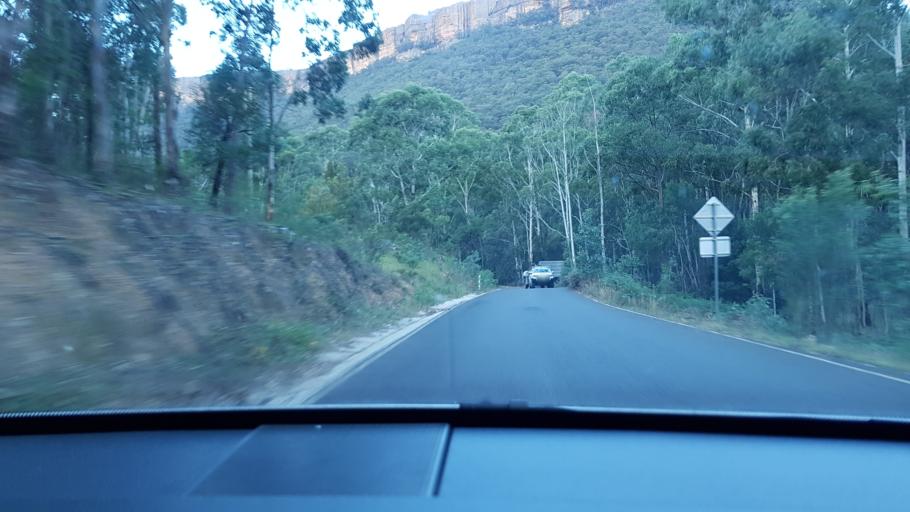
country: AU
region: New South Wales
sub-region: Lithgow
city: Portland
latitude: -33.3047
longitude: 150.1206
